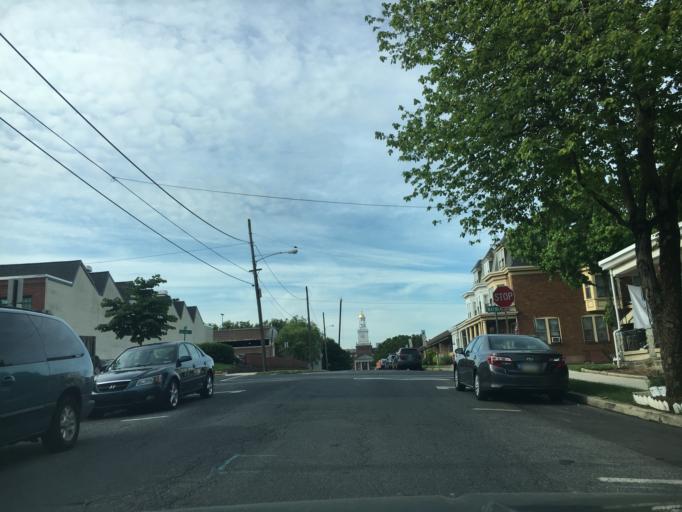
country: US
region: Pennsylvania
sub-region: Berks County
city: West Reading
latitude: 40.3340
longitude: -75.9499
